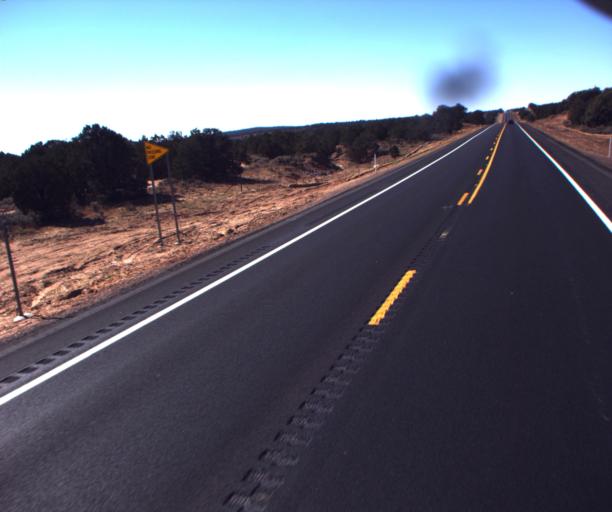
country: US
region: Arizona
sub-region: Apache County
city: Ganado
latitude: 35.7158
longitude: -109.3421
